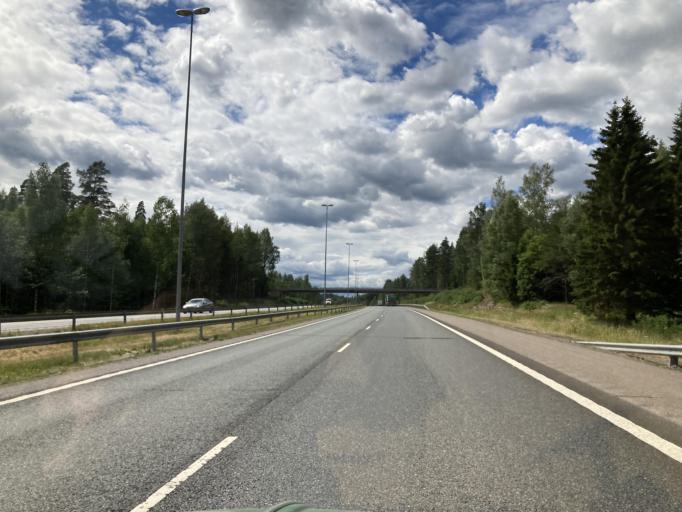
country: FI
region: Uusimaa
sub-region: Helsinki
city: Vihti
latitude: 60.2947
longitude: 24.3501
